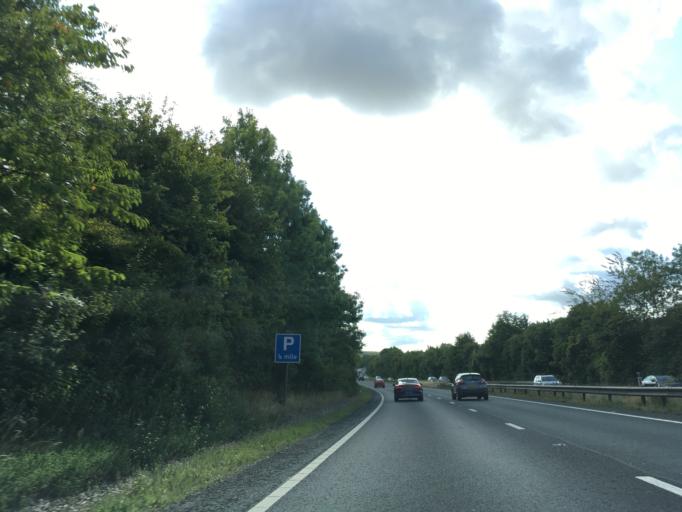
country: GB
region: England
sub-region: Hampshire
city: Highclere
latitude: 51.3261
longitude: -1.3454
